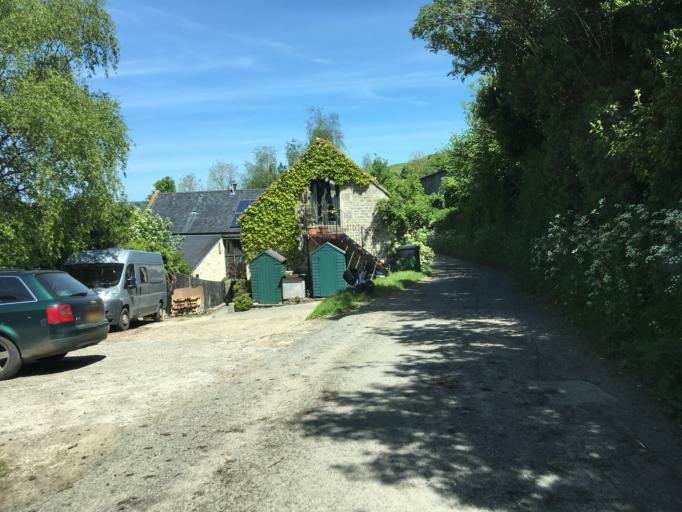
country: GB
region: England
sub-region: Gloucestershire
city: Stroud
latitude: 51.7534
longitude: -2.1879
